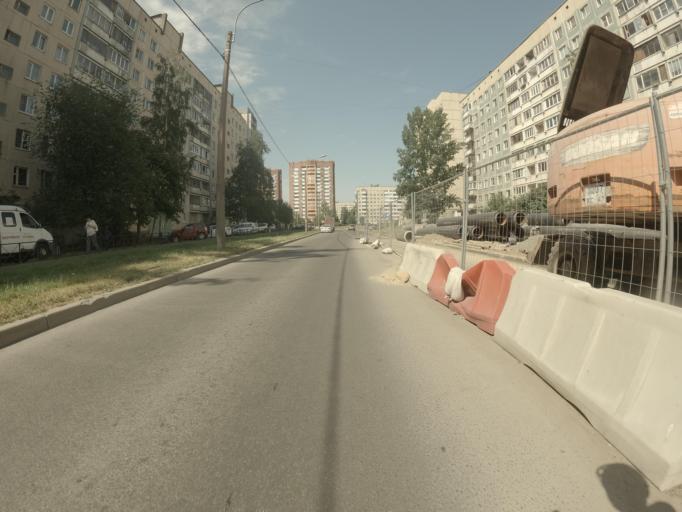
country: RU
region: St.-Petersburg
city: Krasnogvargeisky
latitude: 59.9412
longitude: 30.4800
